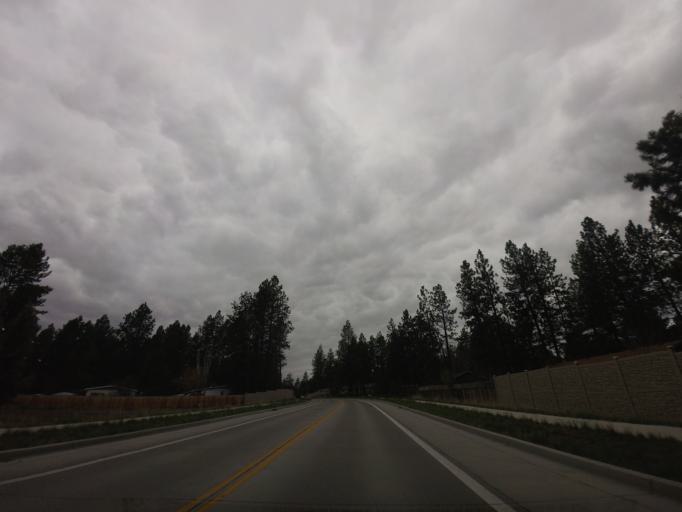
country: US
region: Oregon
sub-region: Deschutes County
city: Bend
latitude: 44.0189
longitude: -121.3246
